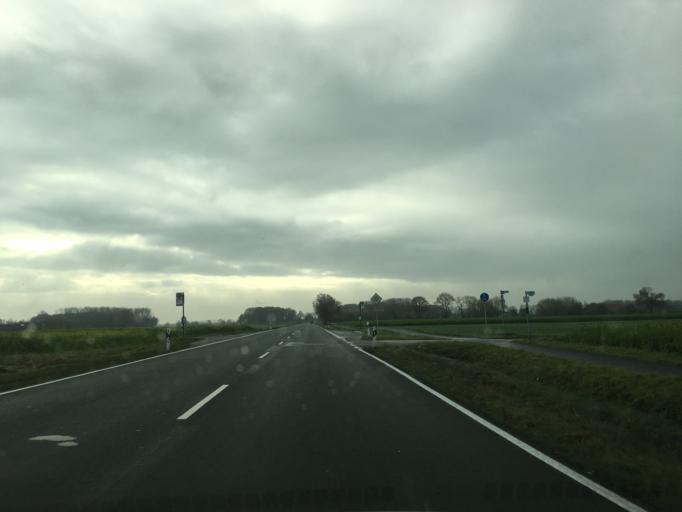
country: DE
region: North Rhine-Westphalia
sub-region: Regierungsbezirk Munster
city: Senden
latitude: 51.8183
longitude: 7.4929
